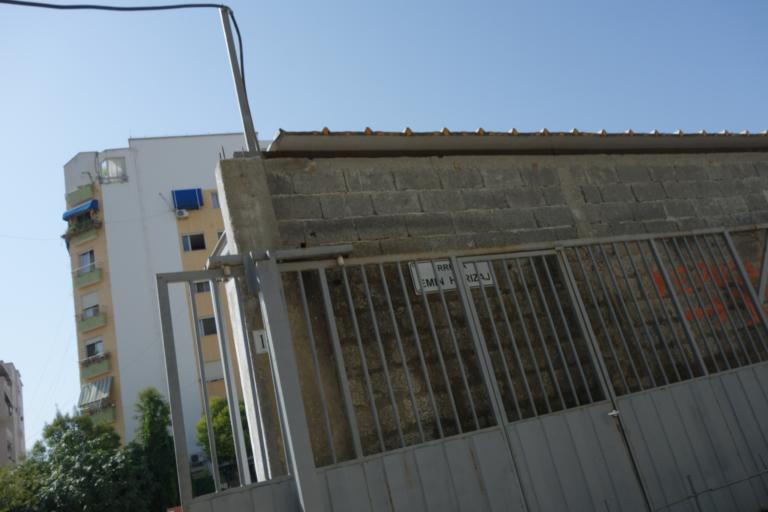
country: AL
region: Tirane
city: Tirana
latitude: 41.3274
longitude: 19.8388
